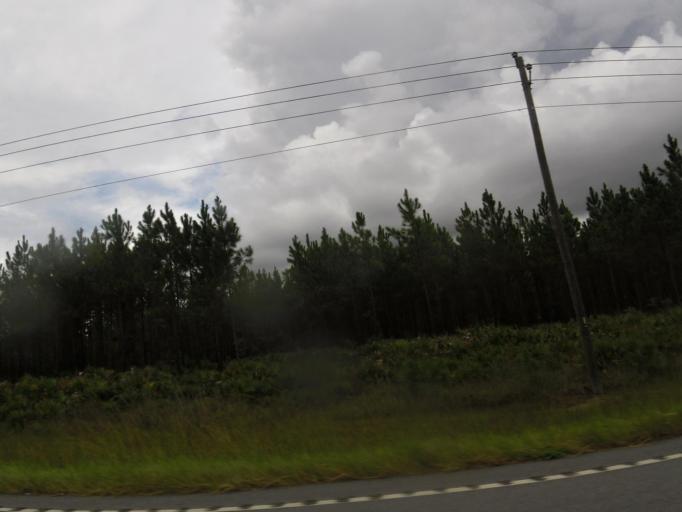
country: US
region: Florida
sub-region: Baker County
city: Macclenny
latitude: 30.5183
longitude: -82.1265
